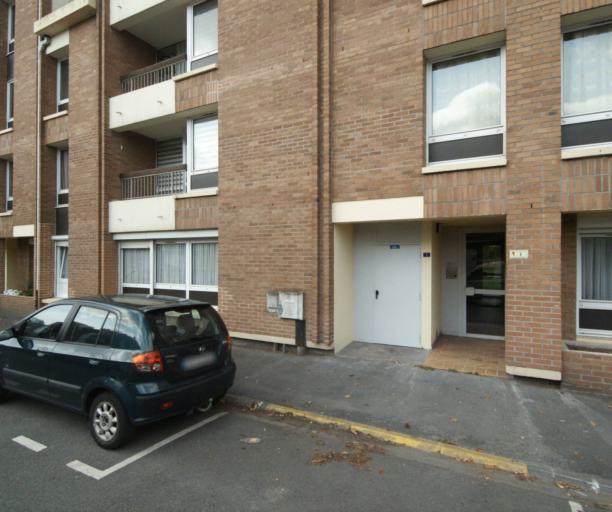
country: FR
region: Nord-Pas-de-Calais
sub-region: Departement du Nord
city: Lys-lez-Lannoy
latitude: 50.6692
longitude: 3.2135
